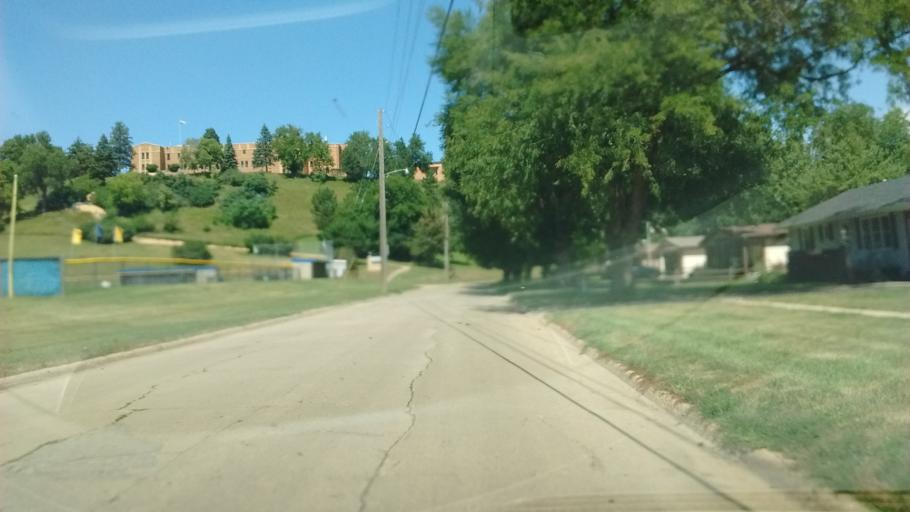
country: US
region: Iowa
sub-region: Woodbury County
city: Sioux City
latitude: 42.5242
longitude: -96.4256
